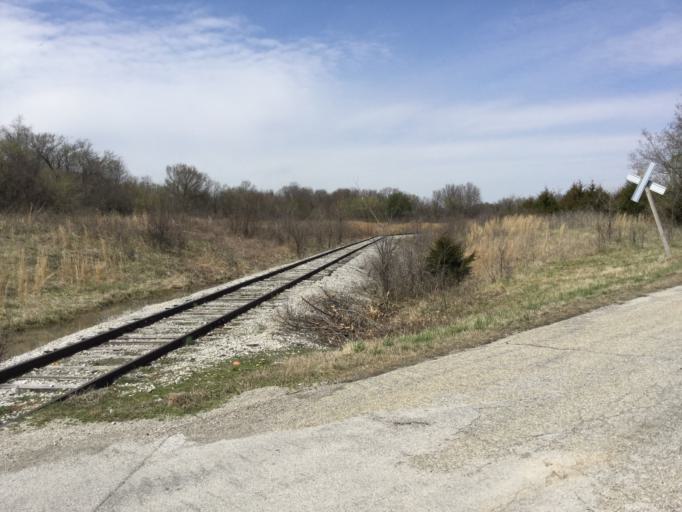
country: US
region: Kansas
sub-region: Cherokee County
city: Galena
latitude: 37.1168
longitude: -94.6795
